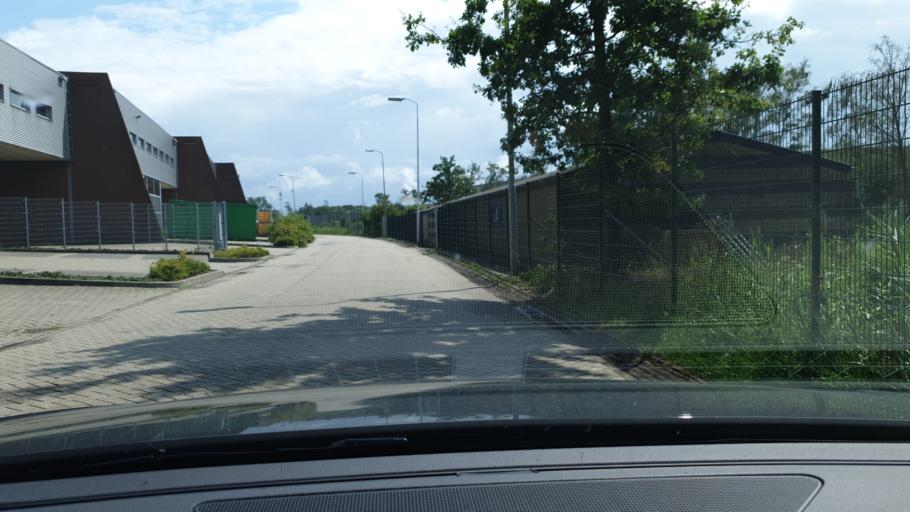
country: NL
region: North Brabant
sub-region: Gemeente Eindhoven
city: Meerhoven
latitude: 51.4364
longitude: 5.4327
